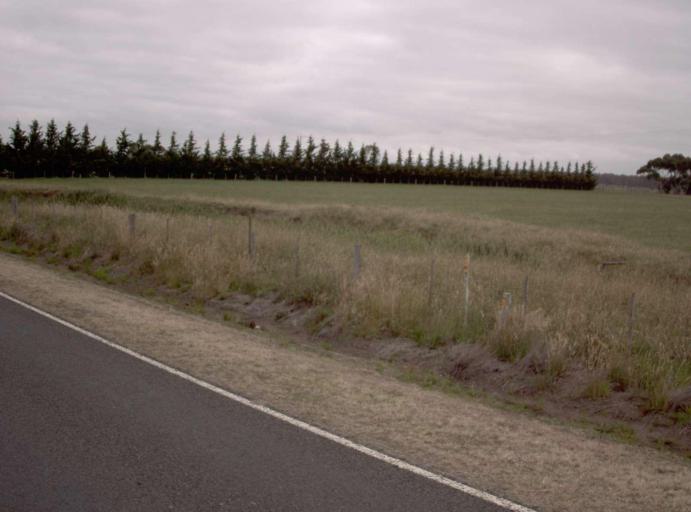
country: AU
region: Victoria
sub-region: Wellington
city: Sale
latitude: -38.0772
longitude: 146.9873
